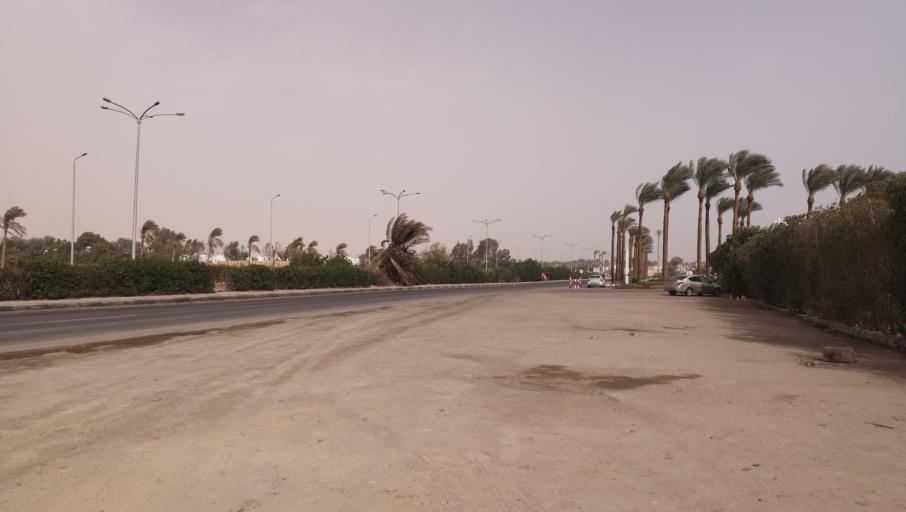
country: EG
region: South Sinai
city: Sharm el-Sheikh
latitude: 27.8668
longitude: 34.3145
